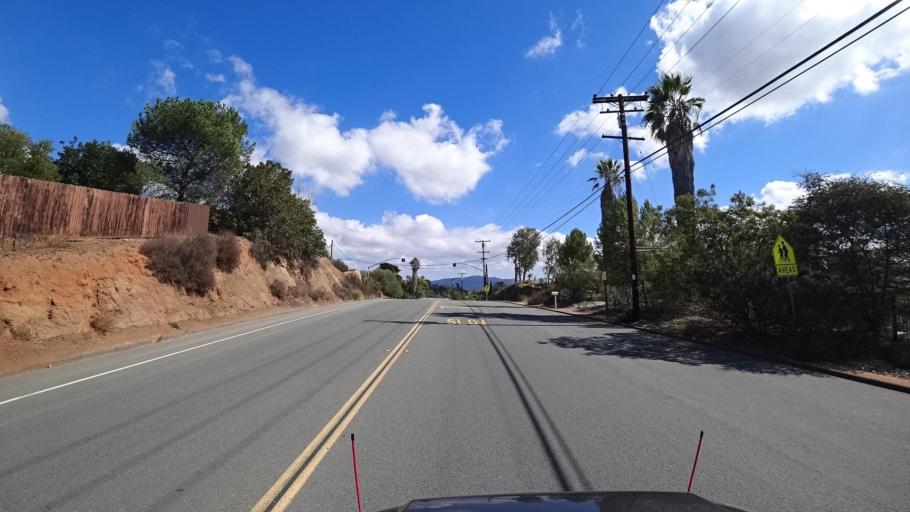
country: US
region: California
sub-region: San Diego County
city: Casa de Oro-Mount Helix
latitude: 32.7622
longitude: -116.9490
